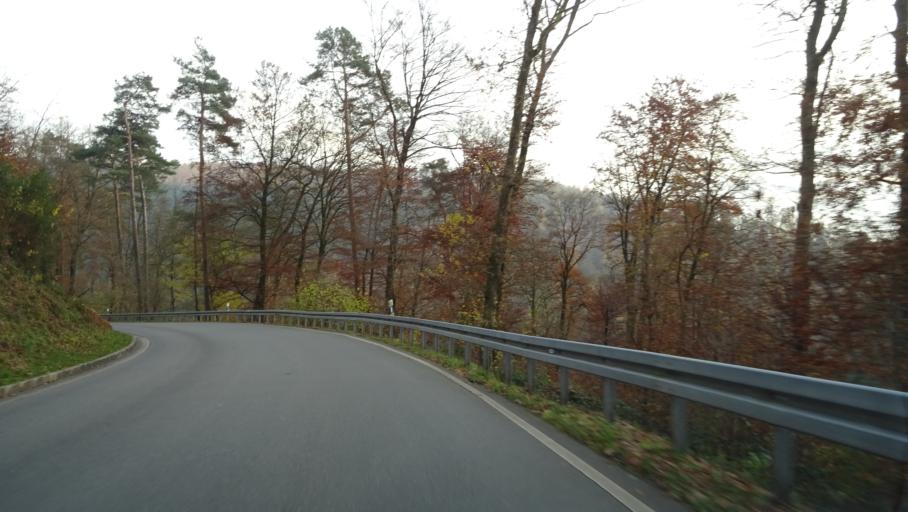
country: DE
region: Baden-Wuerttemberg
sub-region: Karlsruhe Region
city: Neckargerach
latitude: 49.4097
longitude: 9.0794
